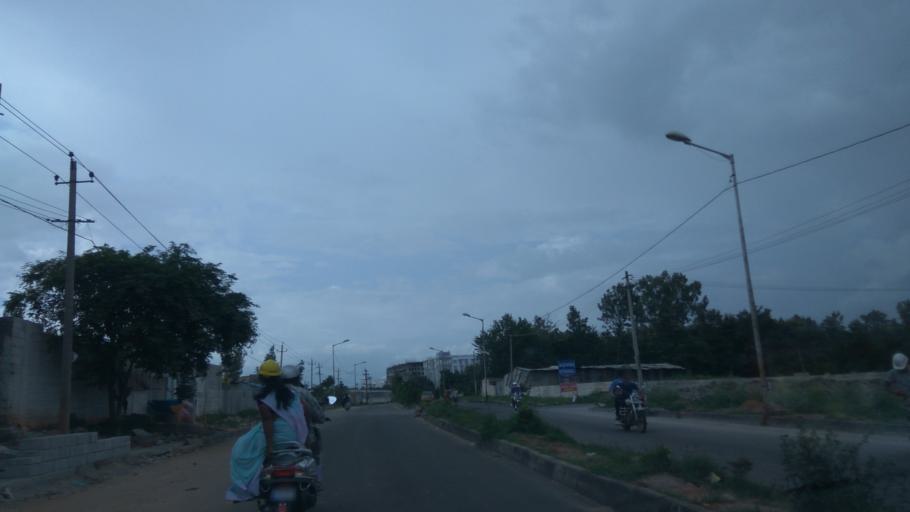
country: IN
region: Karnataka
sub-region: Bangalore Urban
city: Yelahanka
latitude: 13.1095
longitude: 77.6336
